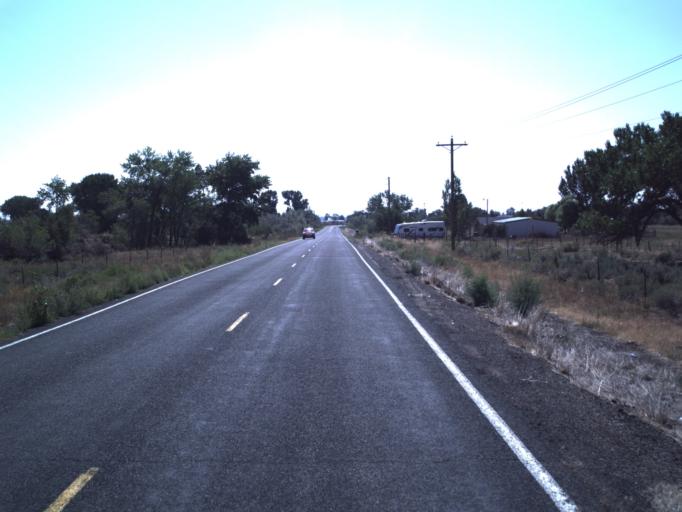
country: US
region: Utah
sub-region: Duchesne County
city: Duchesne
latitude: 40.2877
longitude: -110.2252
